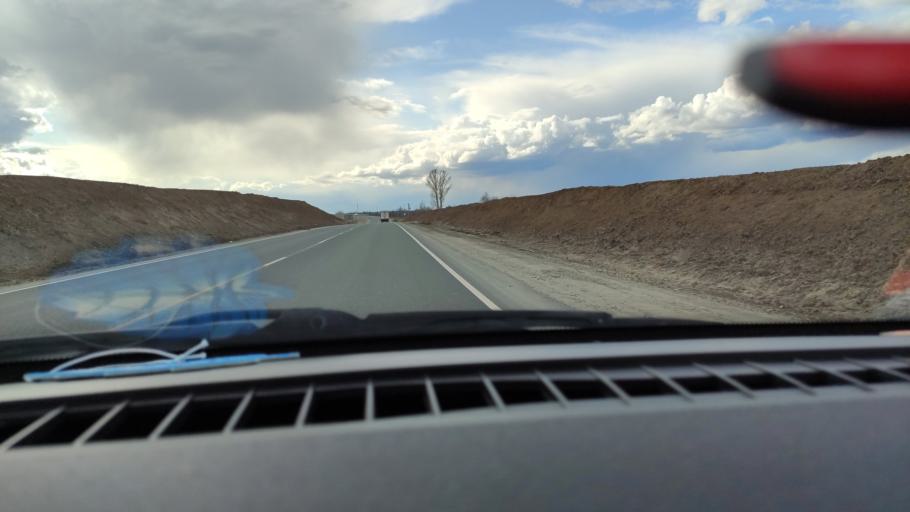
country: RU
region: Saratov
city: Sennoy
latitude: 52.1610
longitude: 47.0499
